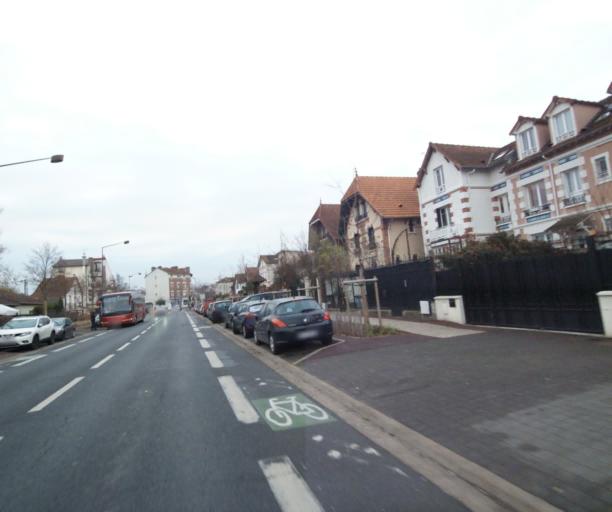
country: FR
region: Ile-de-France
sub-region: Departement des Hauts-de-Seine
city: Rueil-Malmaison
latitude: 48.8837
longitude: 2.1792
